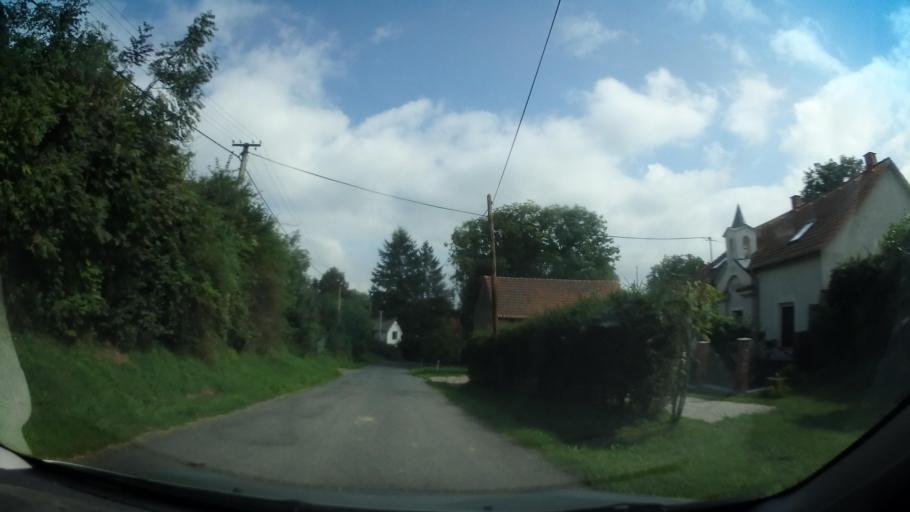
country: CZ
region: Central Bohemia
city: Sedlcany
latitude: 49.7113
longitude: 14.3700
